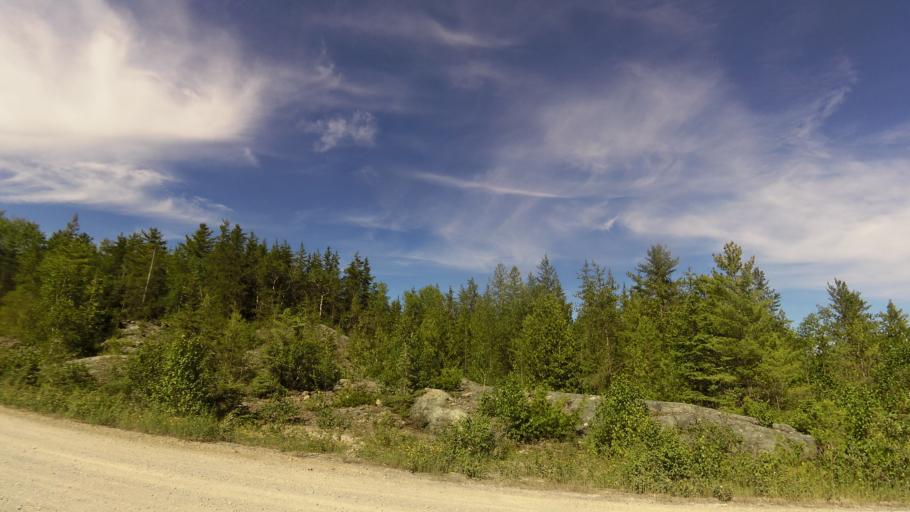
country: CA
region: Ontario
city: Temiskaming Shores
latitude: 47.3840
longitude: -79.6833
